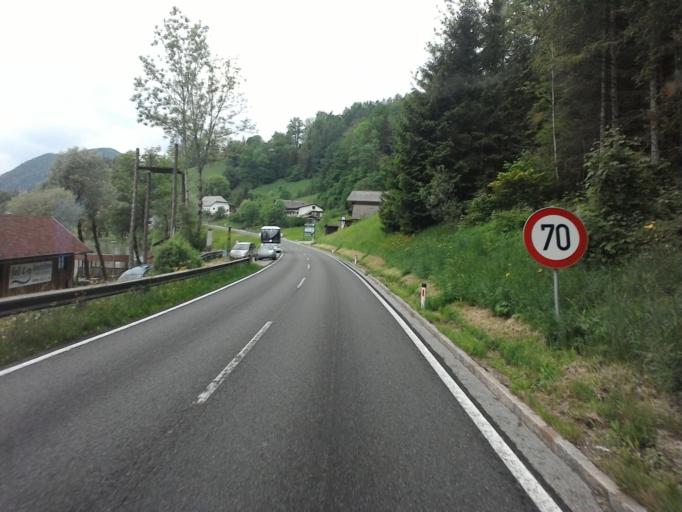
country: AT
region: Upper Austria
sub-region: Politischer Bezirk Steyr-Land
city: Maria Neustift
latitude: 47.8815
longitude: 14.5657
